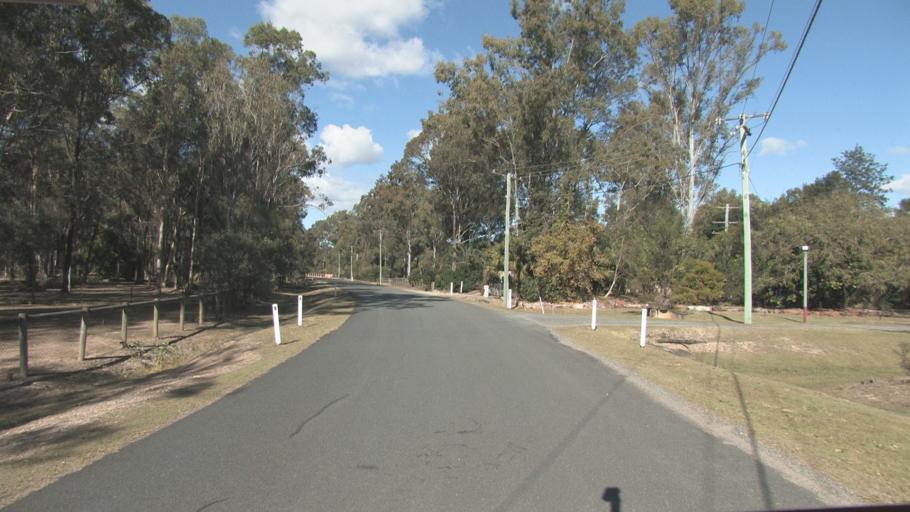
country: AU
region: Queensland
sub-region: Logan
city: Chambers Flat
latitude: -27.7443
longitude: 153.0939
